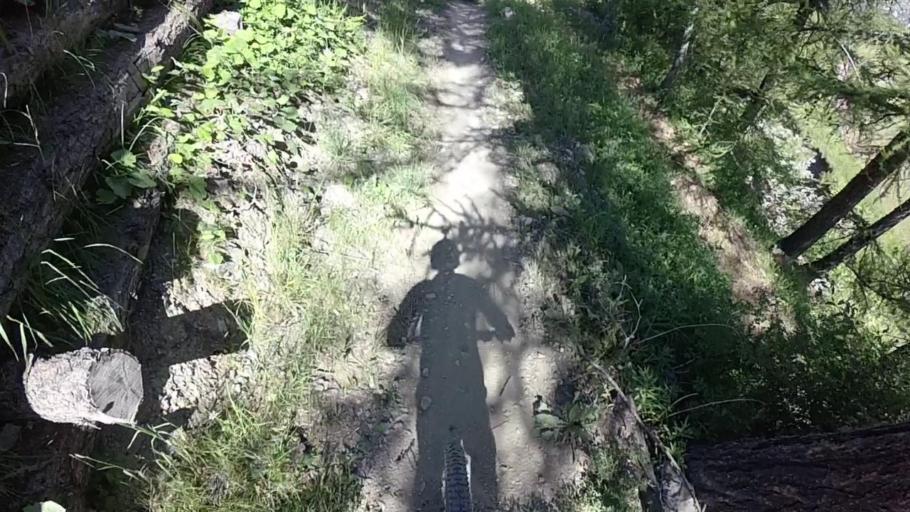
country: FR
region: Provence-Alpes-Cote d'Azur
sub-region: Departement des Hautes-Alpes
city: Embrun
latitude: 44.4865
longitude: 6.5583
